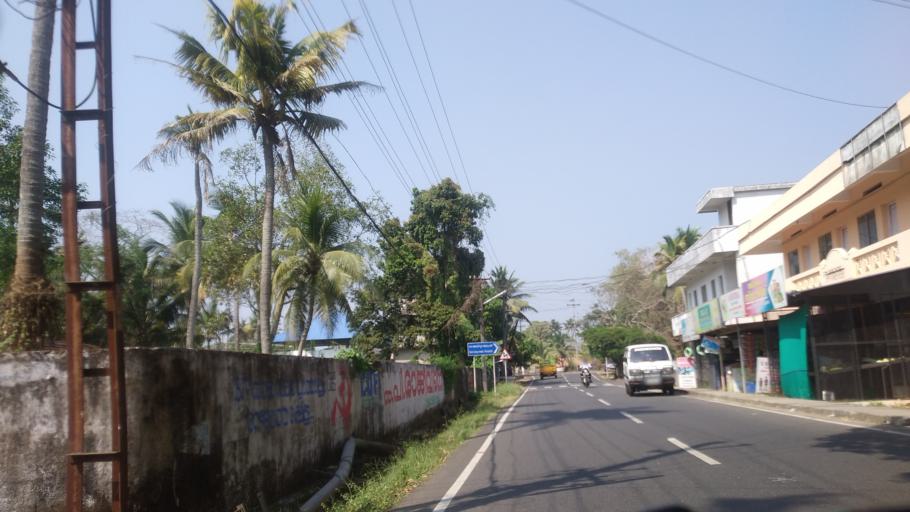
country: IN
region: Kerala
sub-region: Ernakulam
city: Elur
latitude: 10.1350
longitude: 76.2316
